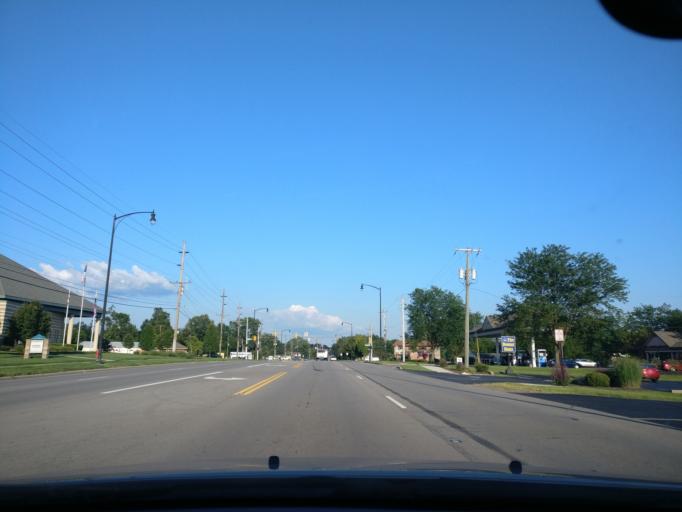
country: US
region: Ohio
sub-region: Warren County
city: Springboro
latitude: 39.5596
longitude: -84.2431
